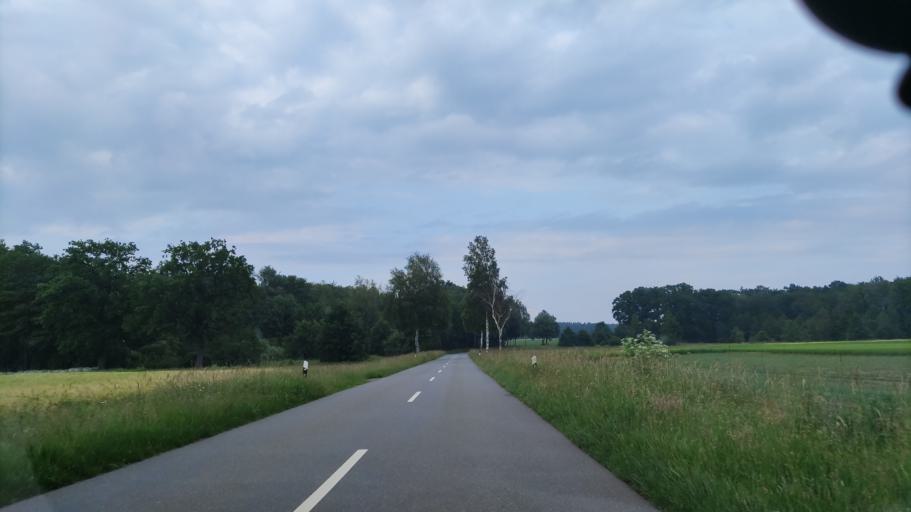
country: DE
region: Lower Saxony
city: Gerdau
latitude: 52.9271
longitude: 10.4209
